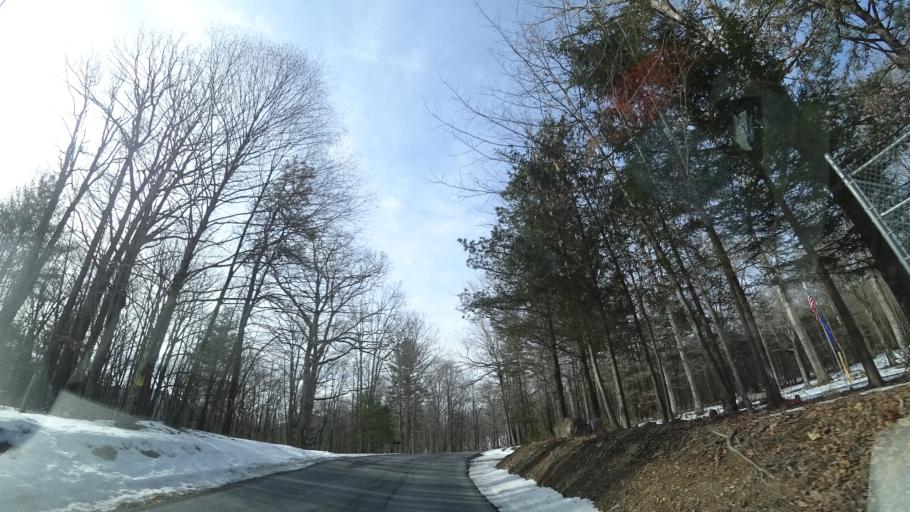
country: US
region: Virginia
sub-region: Shenandoah County
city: Basye
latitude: 38.9517
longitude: -78.6889
